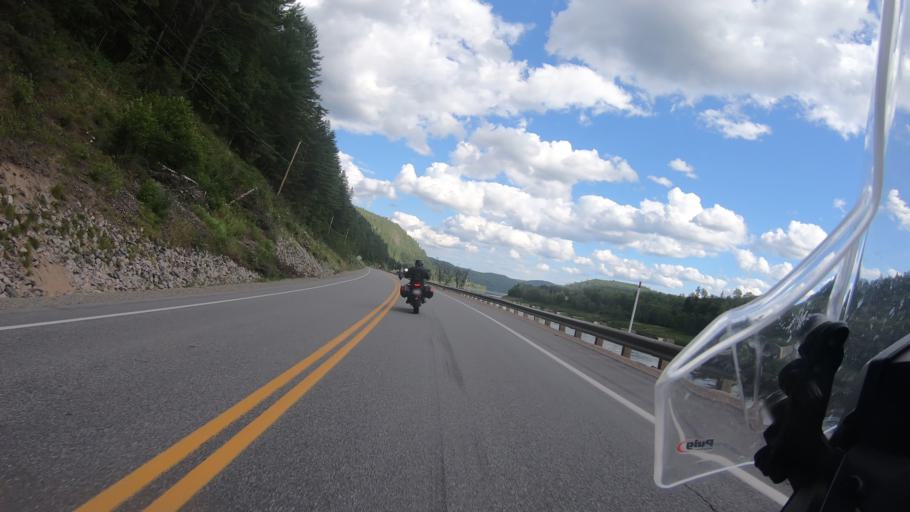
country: CA
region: Quebec
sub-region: Mauricie
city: Saint-Tite
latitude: 46.9983
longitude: -72.9229
